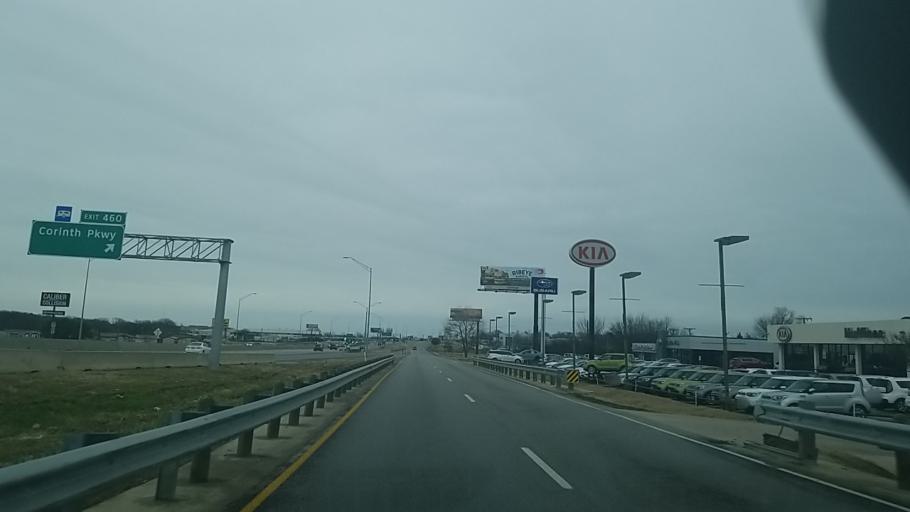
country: US
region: Texas
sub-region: Denton County
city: Corinth
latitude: 33.1603
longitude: -97.0713
